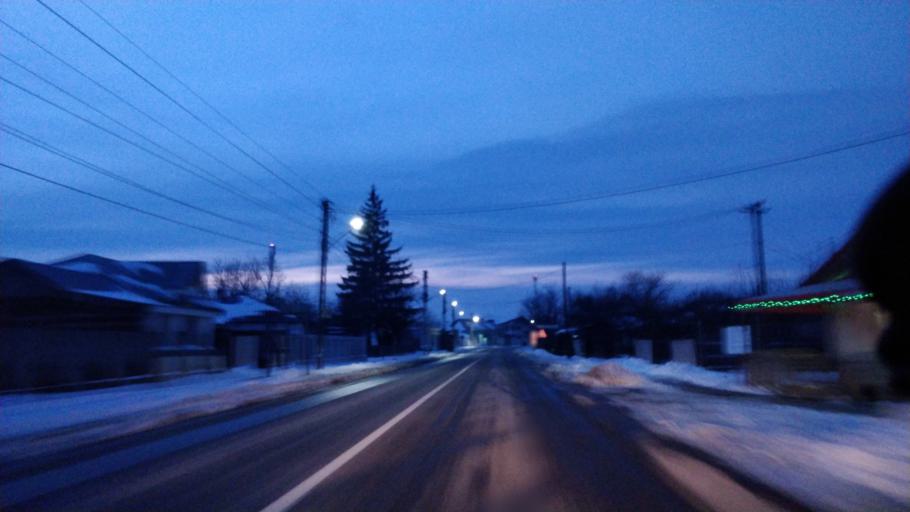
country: RO
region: Vrancea
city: Vulturu de Sus
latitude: 45.6169
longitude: 27.4260
